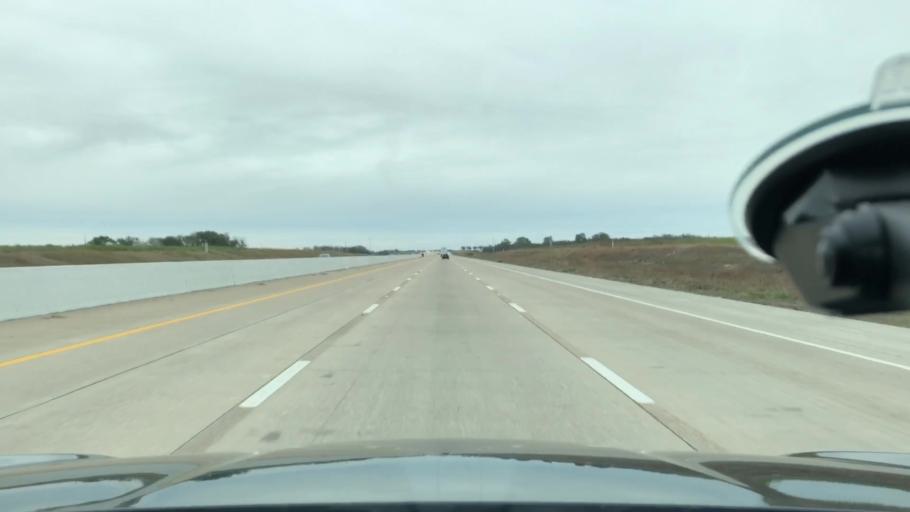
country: US
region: Texas
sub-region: Ellis County
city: Italy
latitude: 32.1530
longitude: -96.9298
